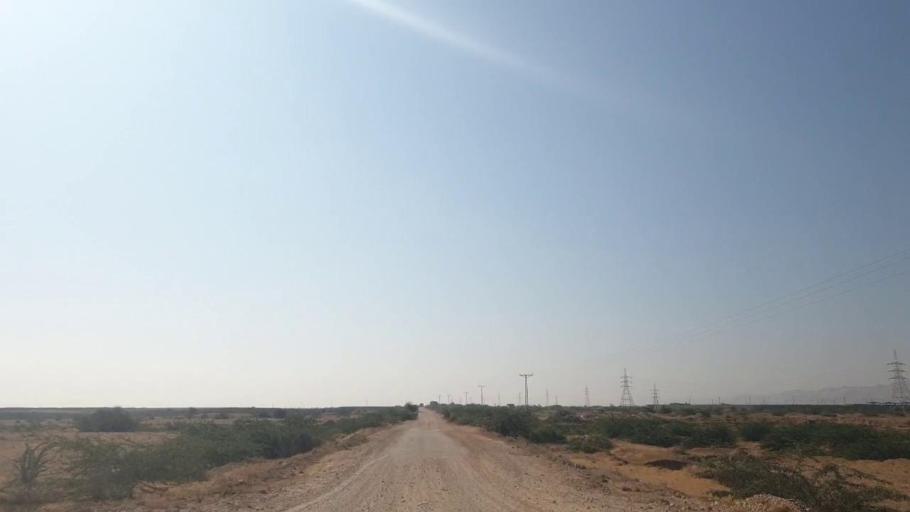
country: PK
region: Sindh
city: Gharo
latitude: 25.1612
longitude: 67.7278
